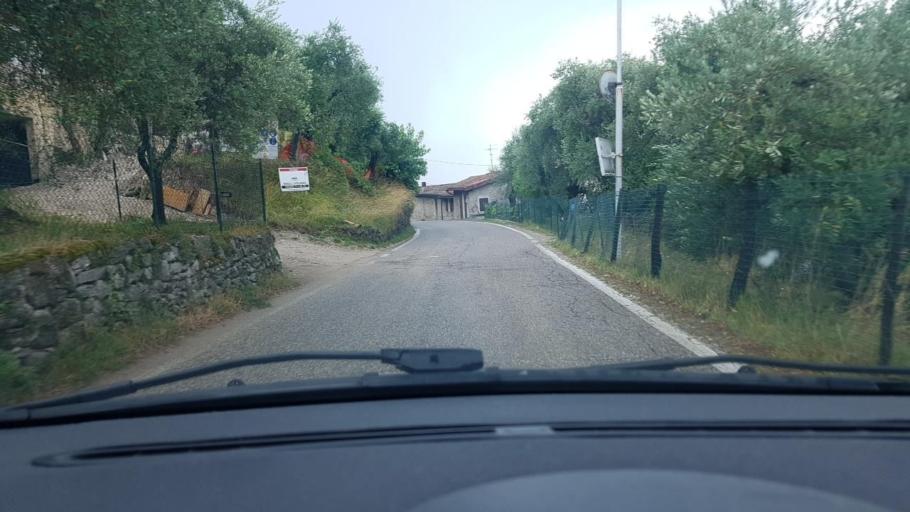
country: IT
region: Veneto
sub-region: Provincia di Verona
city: Torri del Benaco
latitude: 45.6041
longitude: 10.6928
